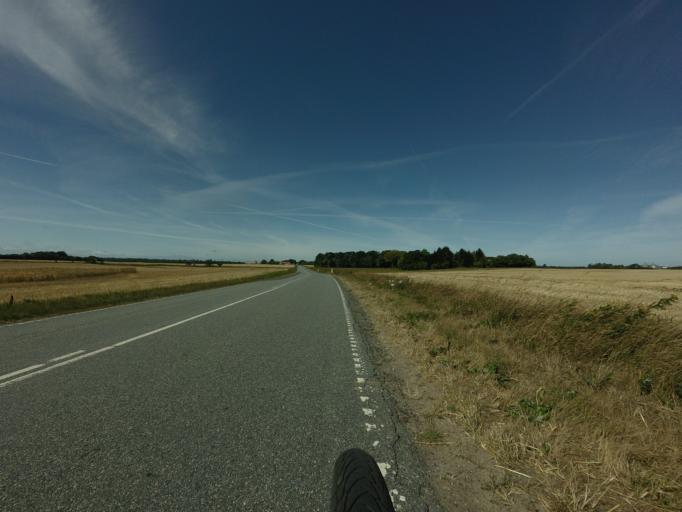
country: DK
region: North Denmark
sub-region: Hjorring Kommune
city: Vra
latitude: 57.3315
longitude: 9.8187
